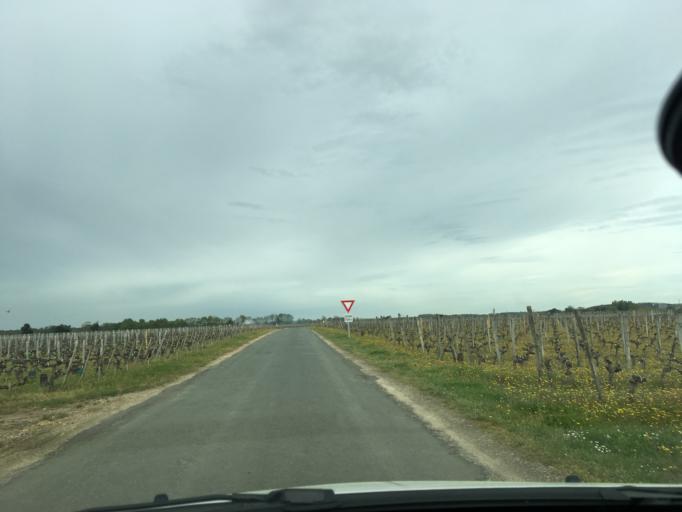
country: FR
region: Aquitaine
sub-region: Departement de la Gironde
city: Lesparre-Medoc
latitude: 45.3252
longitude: -0.8816
